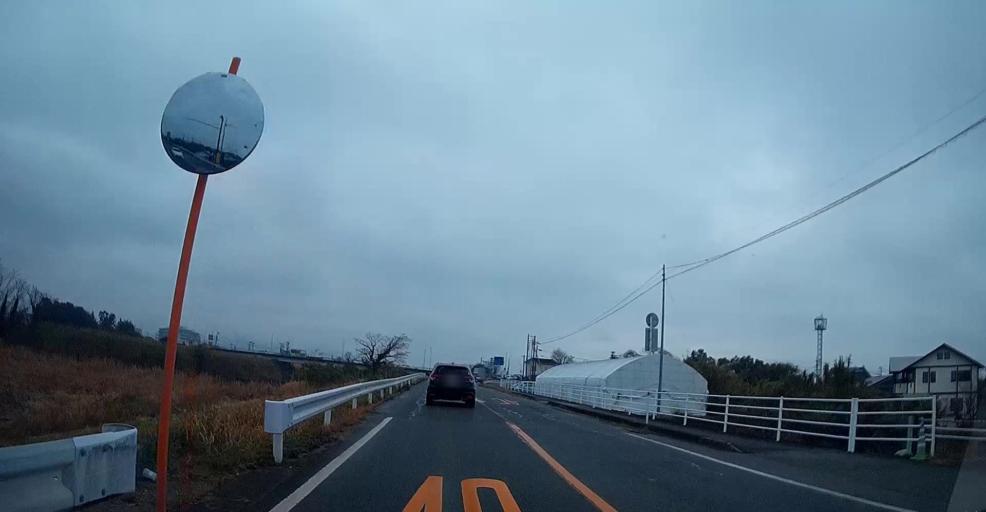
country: JP
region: Kumamoto
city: Kumamoto
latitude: 32.7542
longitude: 130.7396
